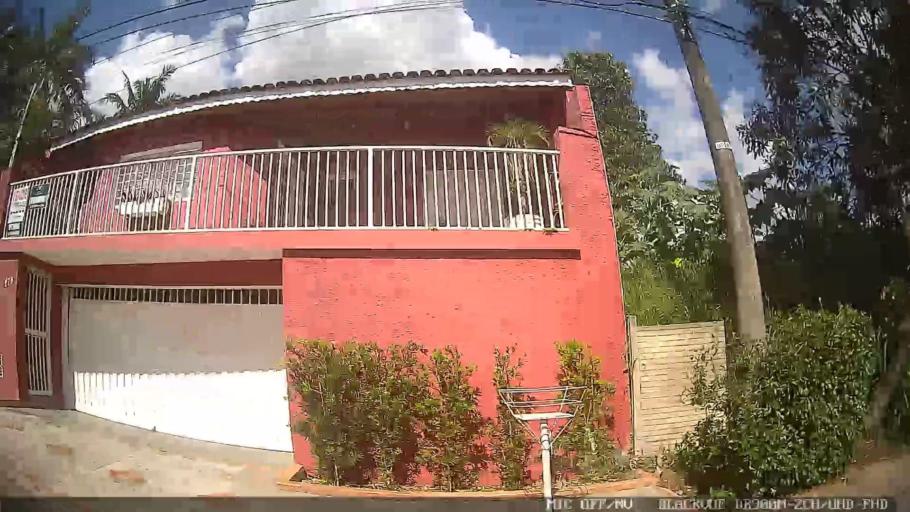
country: BR
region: Sao Paulo
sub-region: Atibaia
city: Atibaia
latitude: -23.1455
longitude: -46.5617
